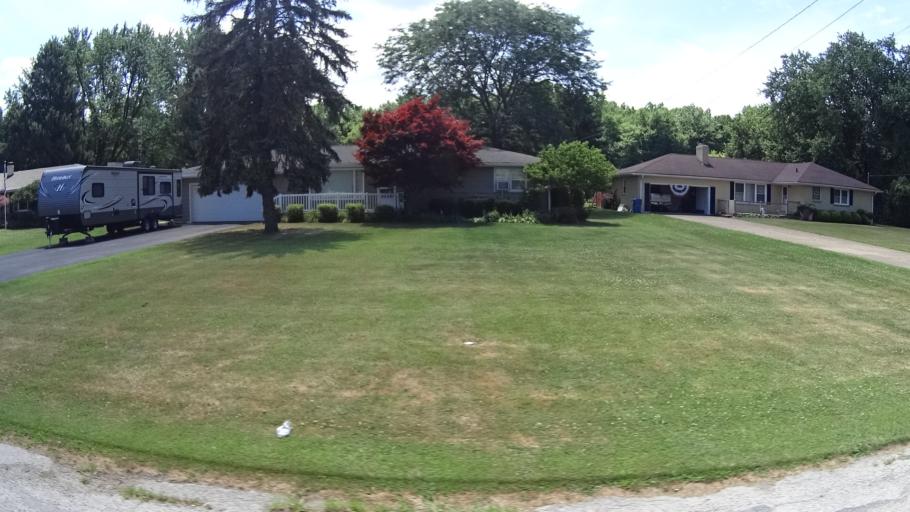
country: US
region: Ohio
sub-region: Erie County
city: Sandusky
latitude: 41.3961
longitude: -82.6797
